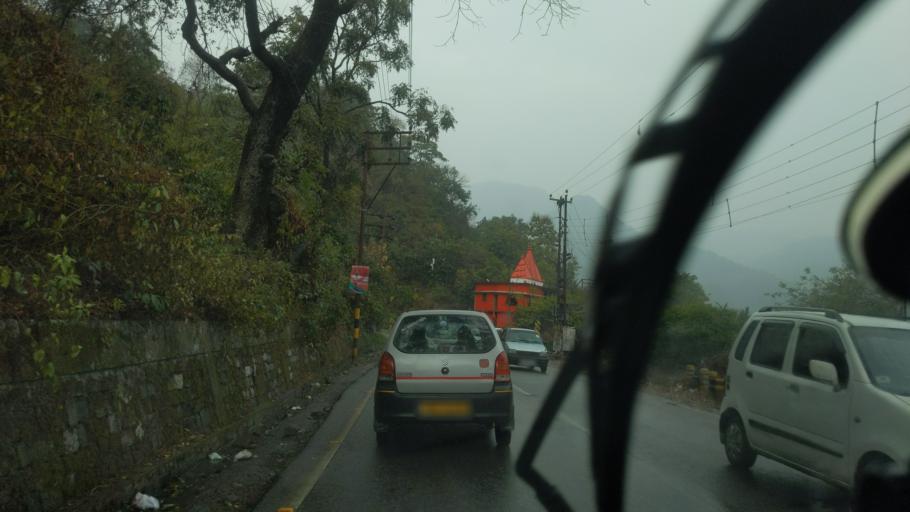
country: IN
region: Uttarakhand
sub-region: Naini Tal
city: Haldwani
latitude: 29.2760
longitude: 79.5455
